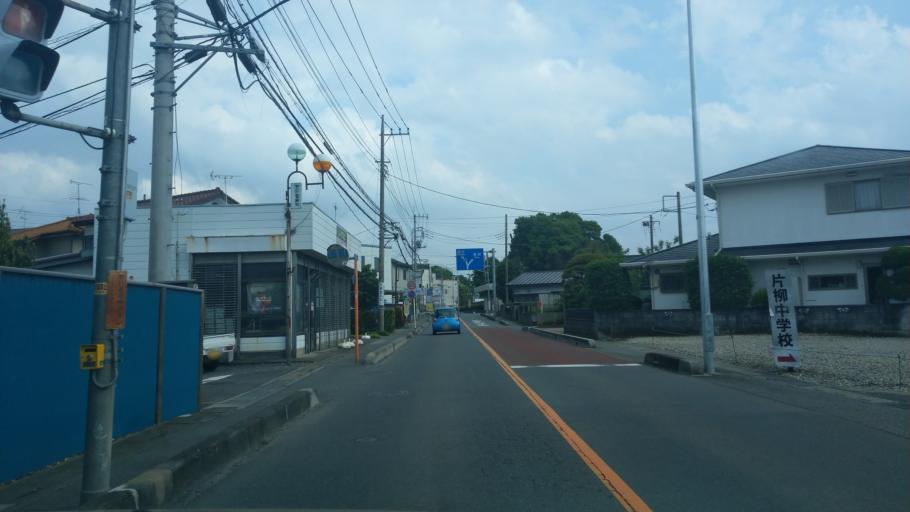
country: JP
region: Saitama
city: Saitama
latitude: 35.9071
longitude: 139.6761
